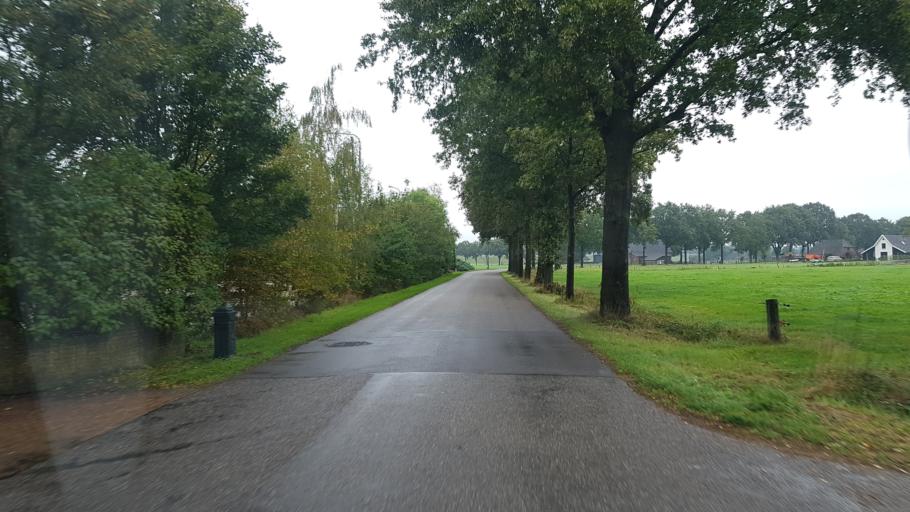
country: NL
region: Gelderland
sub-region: Gemeente Apeldoorn
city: Apeldoorn
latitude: 52.1858
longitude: 6.0305
